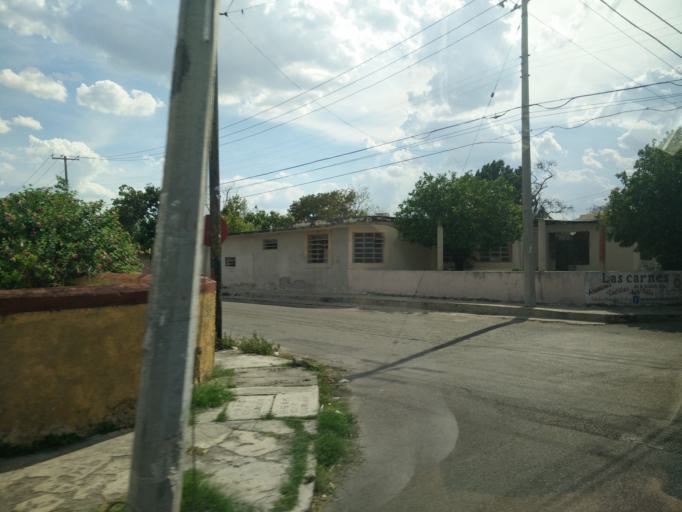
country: MX
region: Yucatan
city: Merida
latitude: 20.9644
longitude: -89.5923
